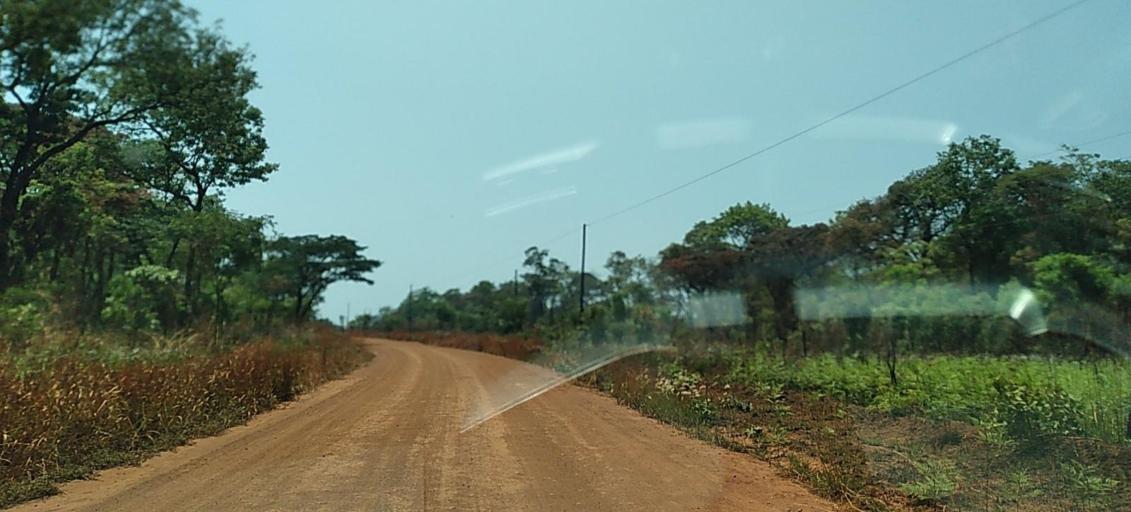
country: CD
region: Katanga
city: Kipushi
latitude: -11.9861
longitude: 26.8715
